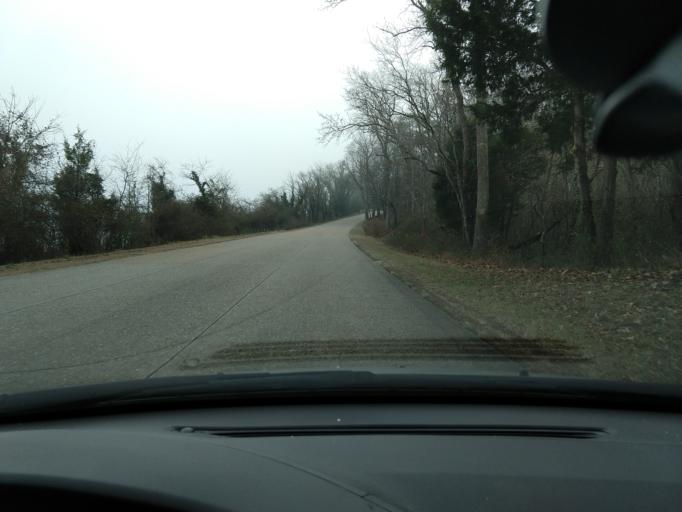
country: US
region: Virginia
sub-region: York County
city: Yorktown
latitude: 37.2505
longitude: -76.5354
